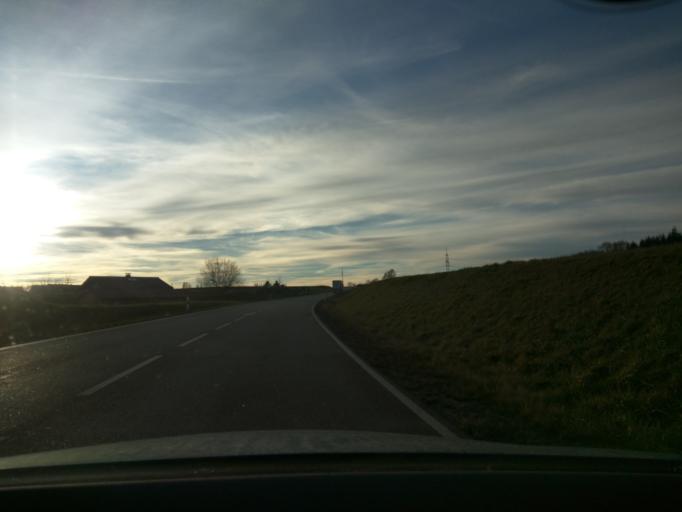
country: DE
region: Bavaria
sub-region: Upper Bavaria
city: Au in der Hallertau
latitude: 48.5656
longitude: 11.7390
